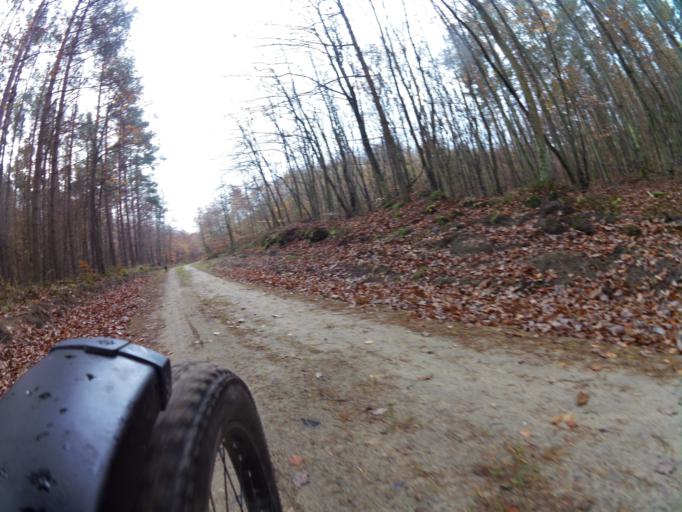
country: PL
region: Pomeranian Voivodeship
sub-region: Powiat pucki
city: Krokowa
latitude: 54.7776
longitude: 18.0919
